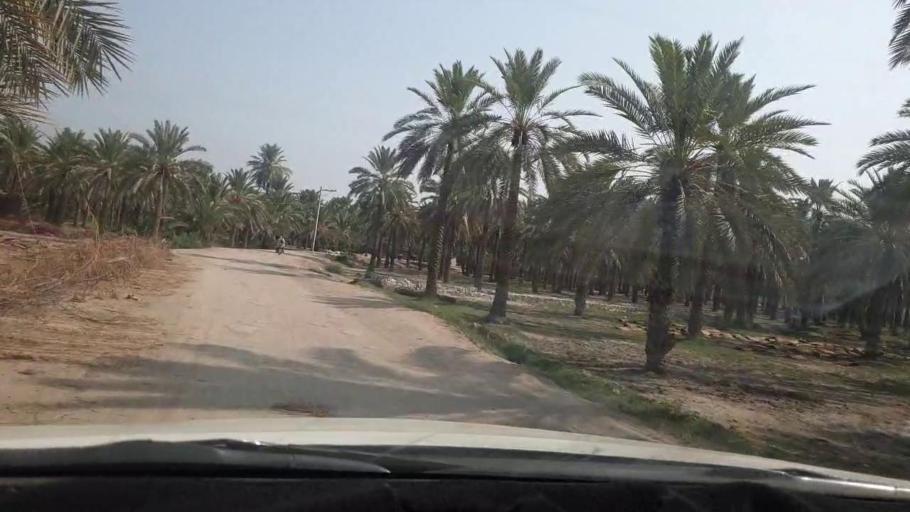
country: PK
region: Sindh
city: Rohri
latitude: 27.5933
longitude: 68.8818
